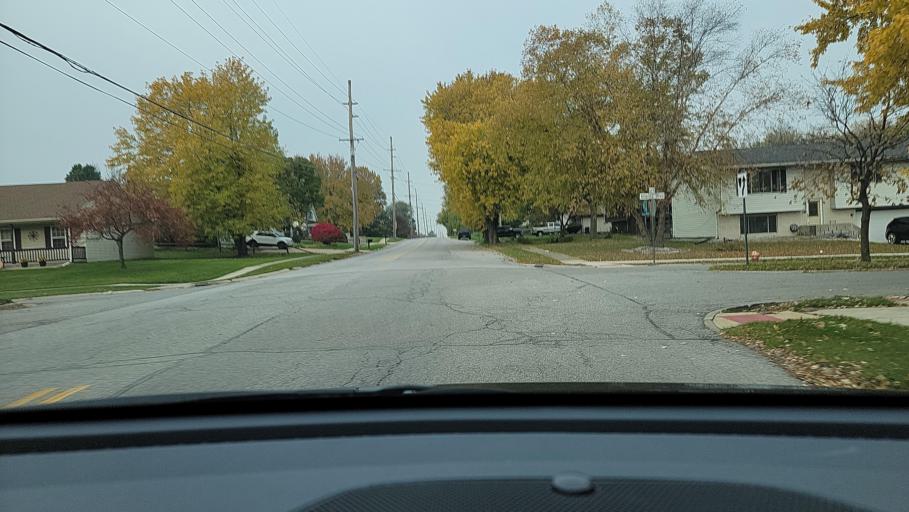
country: US
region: Indiana
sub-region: Porter County
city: Portage
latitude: 41.5578
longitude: -87.1694
